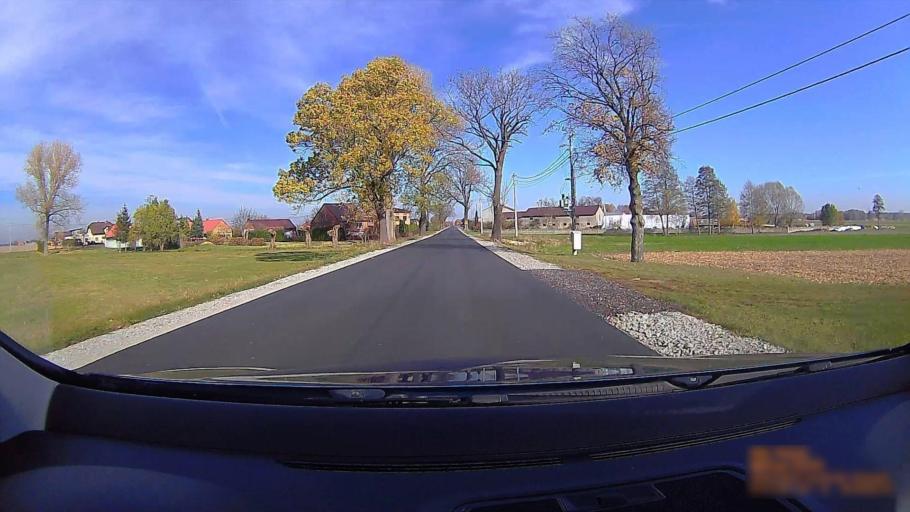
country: PL
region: Greater Poland Voivodeship
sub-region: Powiat ostrzeszowski
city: Doruchow
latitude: 51.4024
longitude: 18.0663
